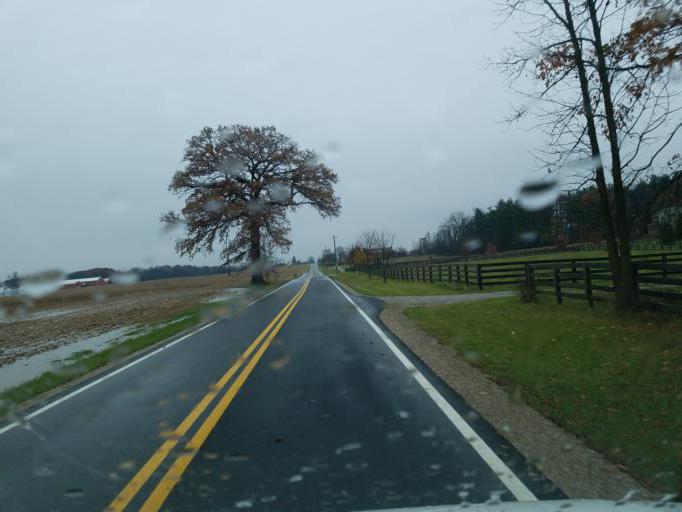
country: US
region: Ohio
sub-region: Knox County
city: Centerburg
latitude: 40.3151
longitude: -82.7596
